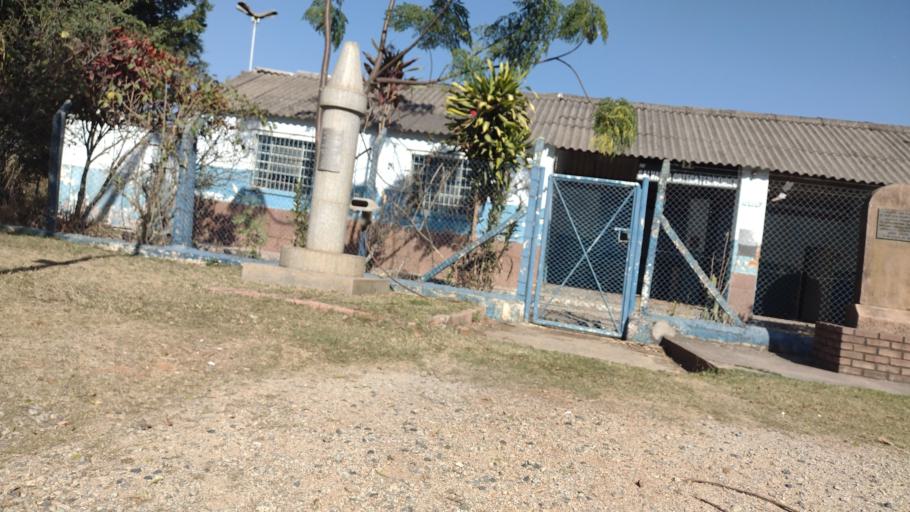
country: BR
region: Sao Paulo
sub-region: Sorocaba
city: Sorocaba
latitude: -23.4111
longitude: -47.4785
